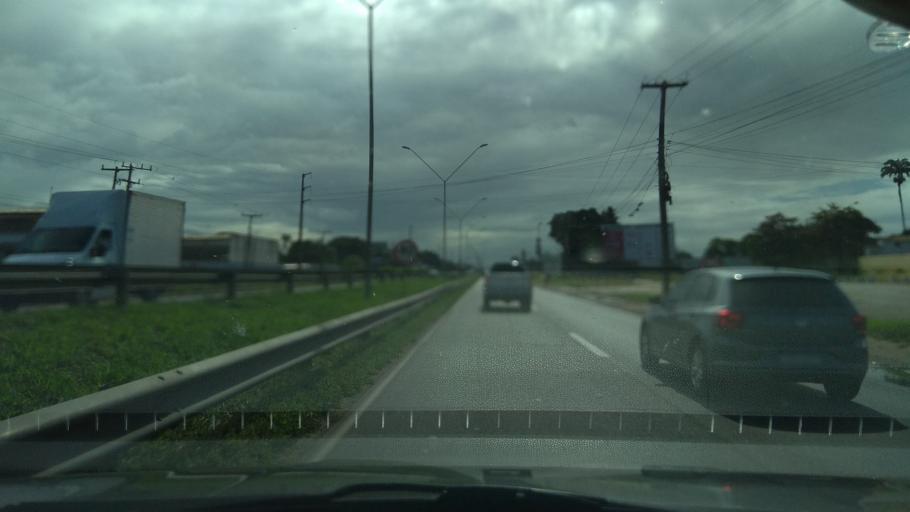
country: BR
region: Bahia
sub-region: Feira De Santana
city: Feira de Santana
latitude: -12.3085
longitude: -38.8879
